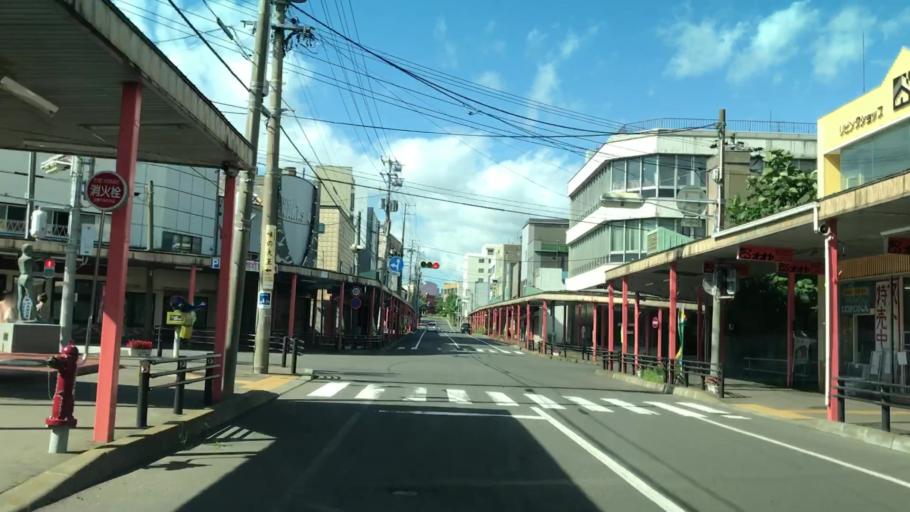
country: JP
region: Hokkaido
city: Muroran
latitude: 42.3179
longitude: 140.9710
